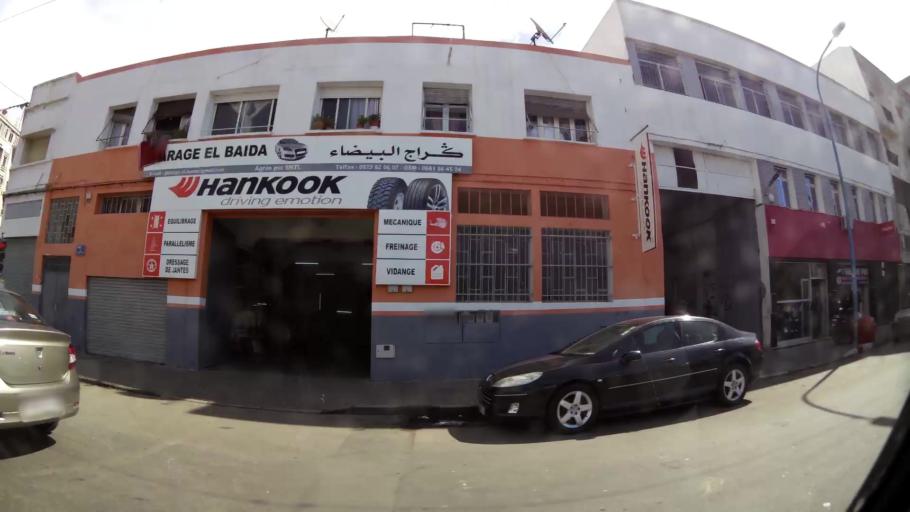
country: MA
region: Grand Casablanca
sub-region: Casablanca
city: Casablanca
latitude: 33.5831
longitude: -7.5815
